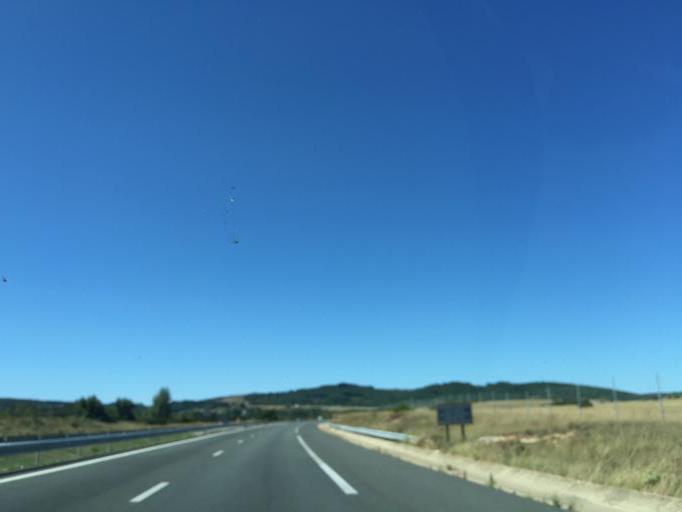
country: FR
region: Midi-Pyrenees
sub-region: Departement de l'Aveyron
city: La Cavalerie
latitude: 43.9563
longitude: 3.2120
